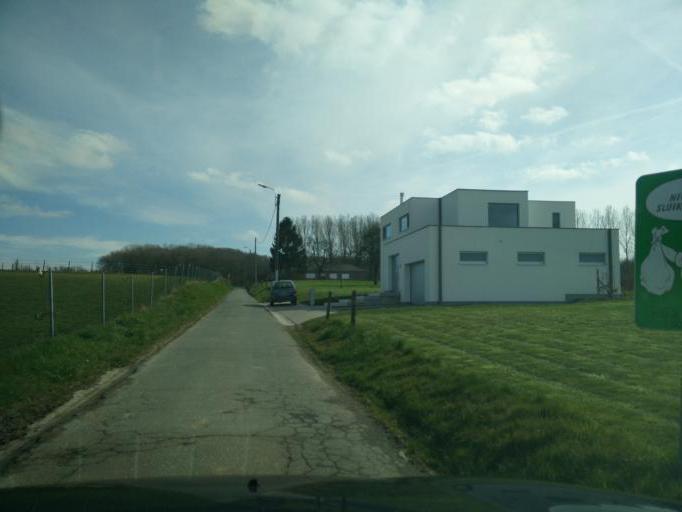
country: BE
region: Flanders
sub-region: Provincie Vlaams-Brabant
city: Ledeberg
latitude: 50.8227
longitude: 4.0765
